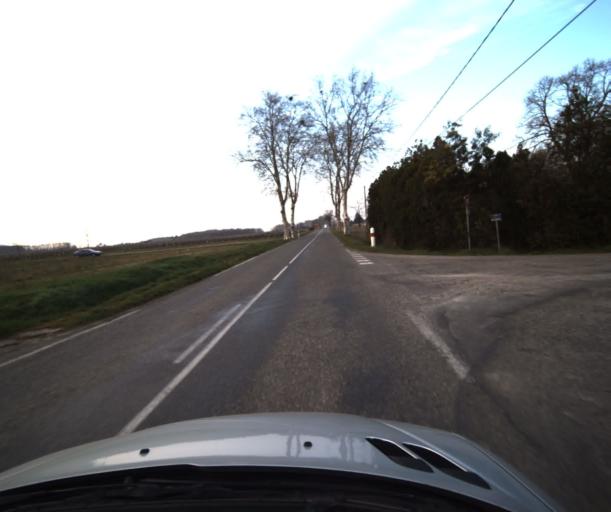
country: FR
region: Midi-Pyrenees
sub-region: Departement de la Haute-Garonne
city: Fronton
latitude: 43.8733
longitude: 1.3793
